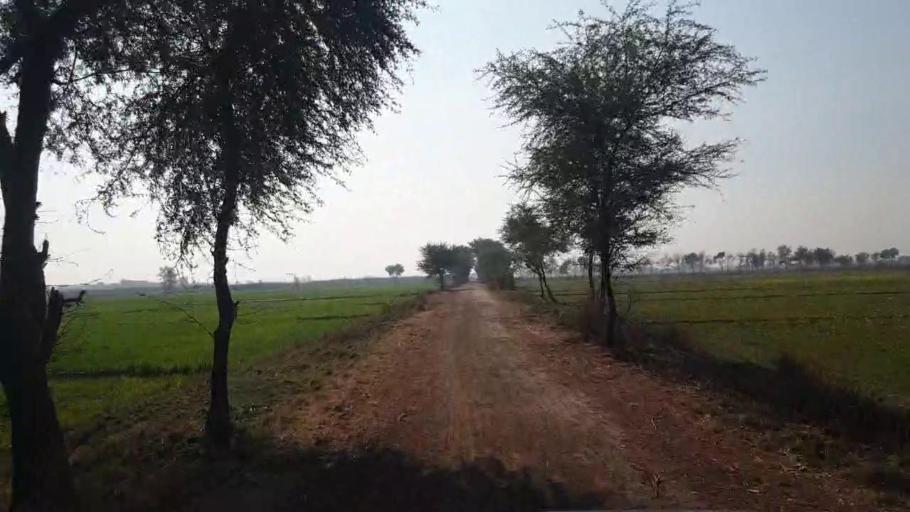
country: PK
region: Sindh
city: Shahdadpur
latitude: 25.9446
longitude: 68.5442
